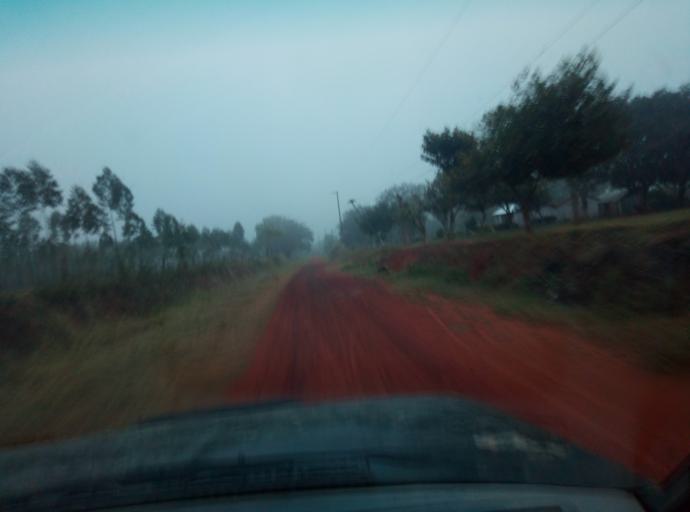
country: PY
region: Caaguazu
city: Doctor Cecilio Baez
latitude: -25.1548
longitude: -56.2888
